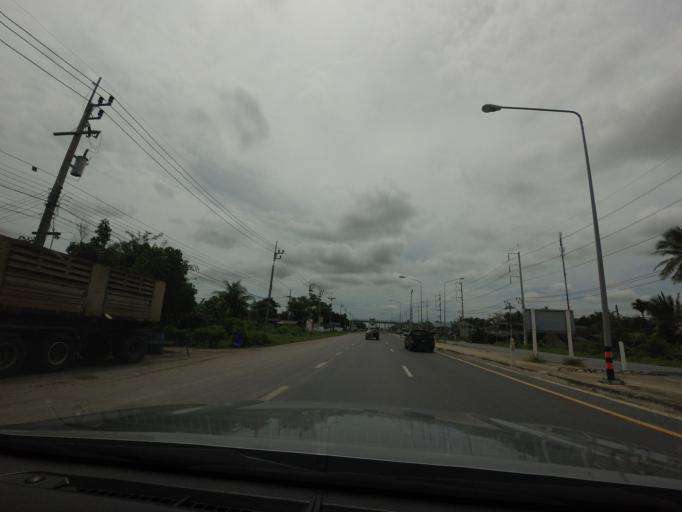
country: TH
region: Nakhon Si Thammarat
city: Hua Sai
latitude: 8.0514
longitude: 100.2145
